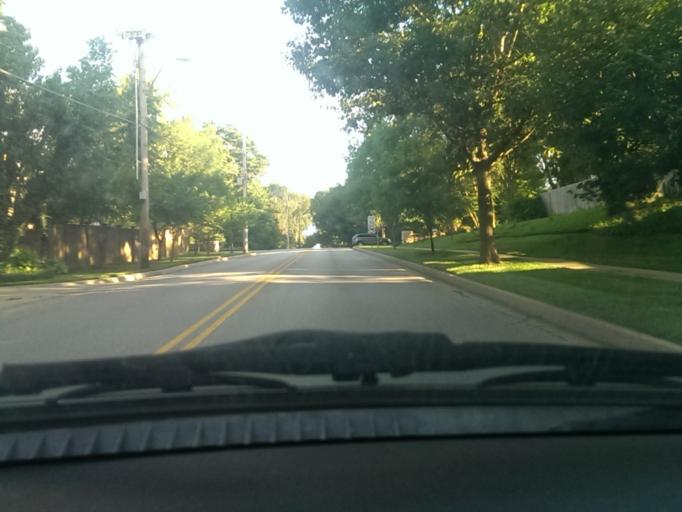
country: US
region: Kansas
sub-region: Johnson County
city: Mission Hills
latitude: 39.0219
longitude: -94.6077
